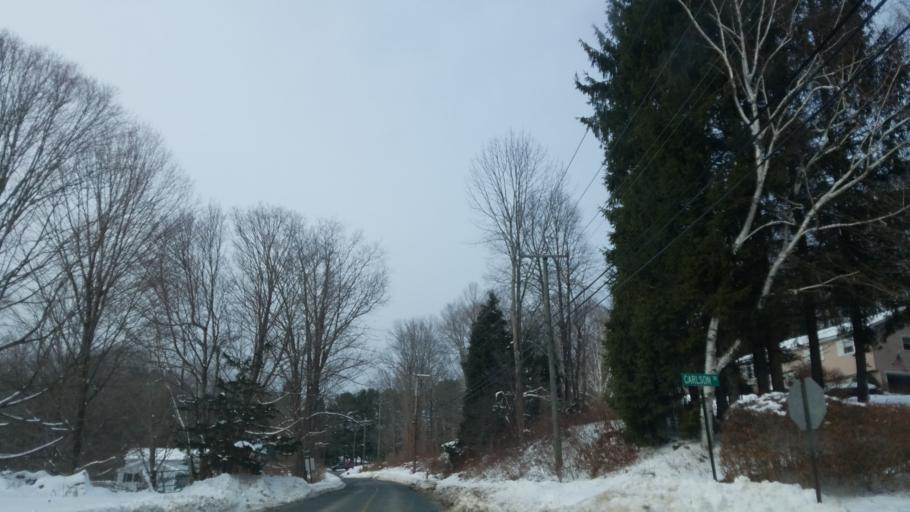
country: US
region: Connecticut
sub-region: Litchfield County
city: Winsted
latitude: 41.8721
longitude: -73.0319
